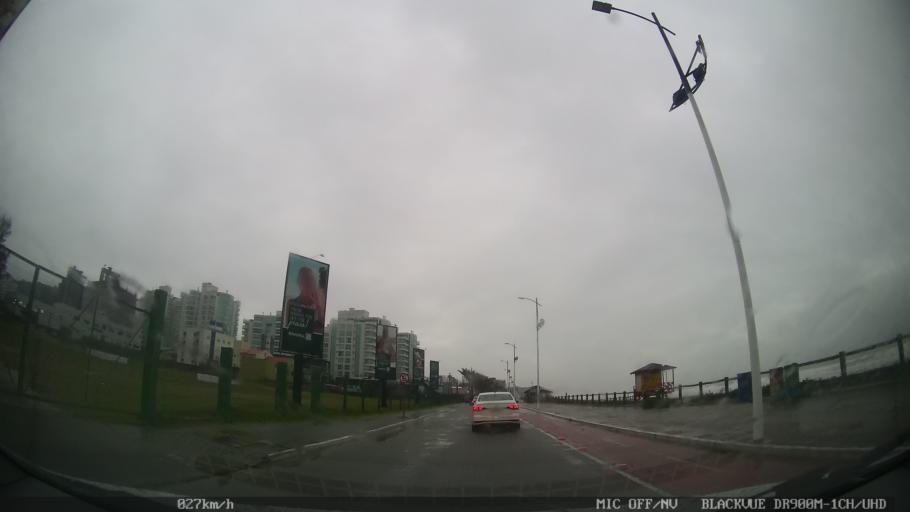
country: BR
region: Santa Catarina
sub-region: Balneario Camboriu
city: Balneario Camboriu
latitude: -26.9543
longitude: -48.6298
